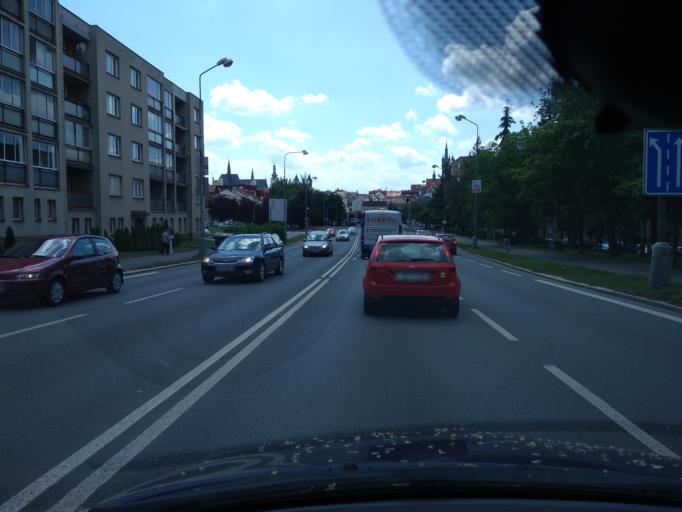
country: CZ
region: Plzensky
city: Klatovy
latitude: 49.4004
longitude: 13.2931
